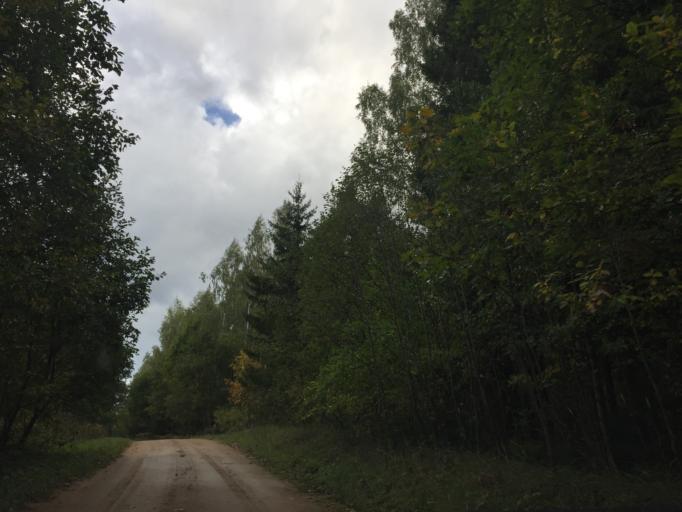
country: LV
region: Amatas Novads
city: Drabesi
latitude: 57.0843
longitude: 25.1731
